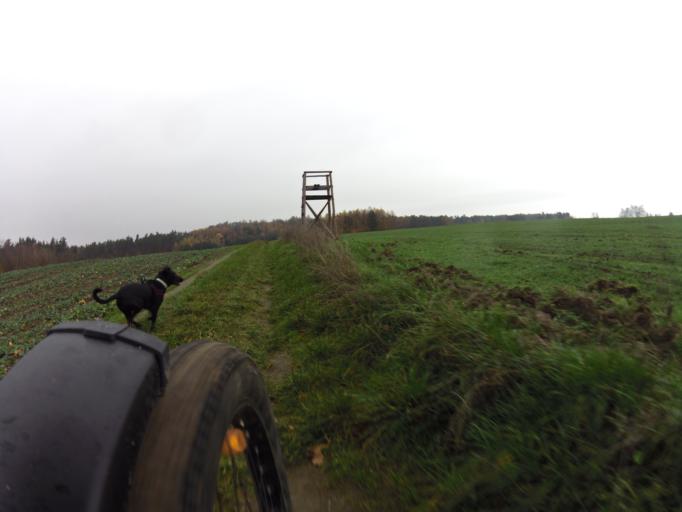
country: PL
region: Pomeranian Voivodeship
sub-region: Powiat pucki
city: Krokowa
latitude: 54.7273
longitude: 18.1318
